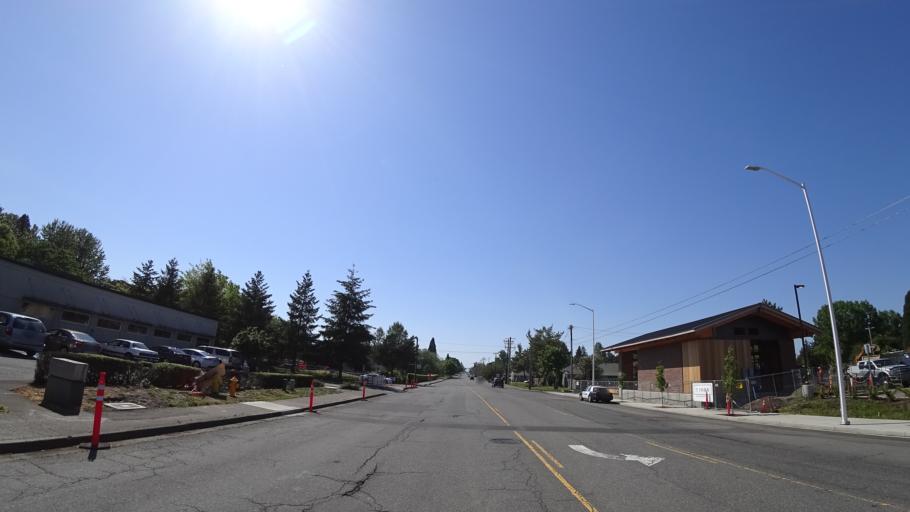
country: US
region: Oregon
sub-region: Washington County
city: Cedar Hills
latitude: 45.4996
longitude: -122.8100
